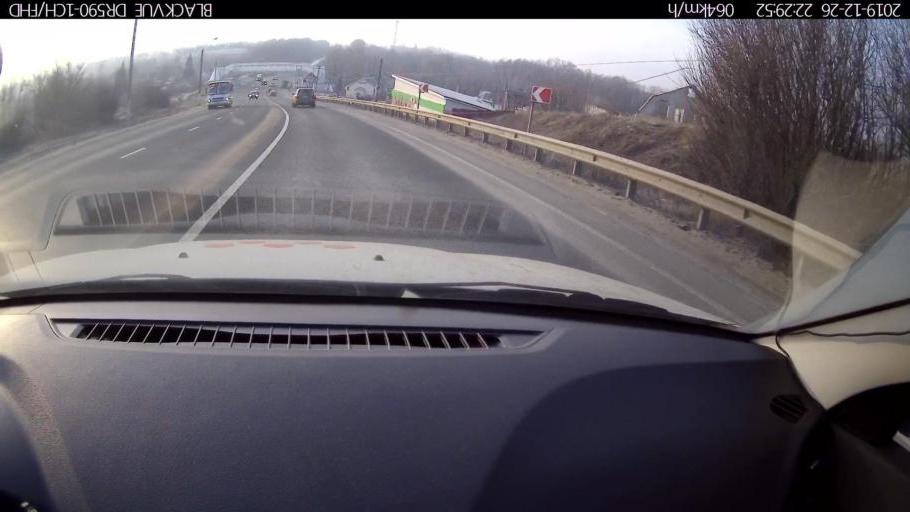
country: RU
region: Nizjnij Novgorod
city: Burevestnik
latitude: 56.1771
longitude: 43.7711
